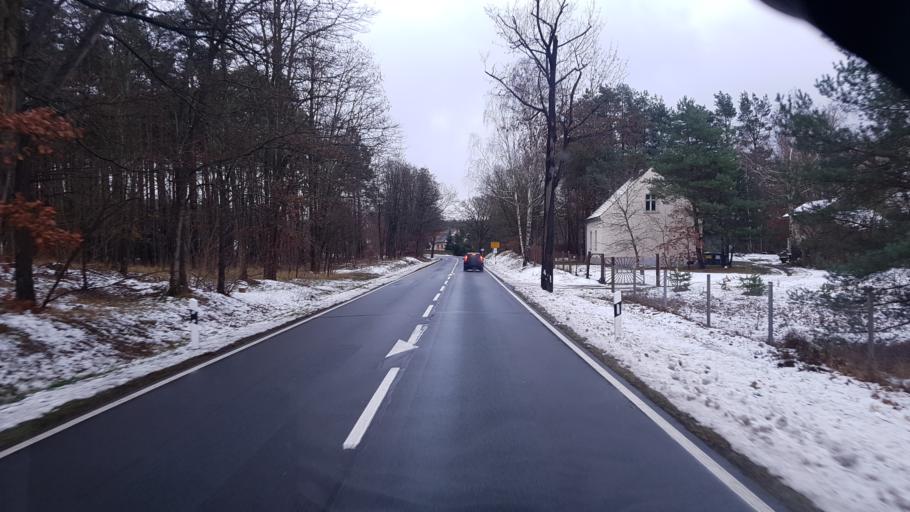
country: DE
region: Brandenburg
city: Jamlitz
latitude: 51.9861
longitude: 14.4054
